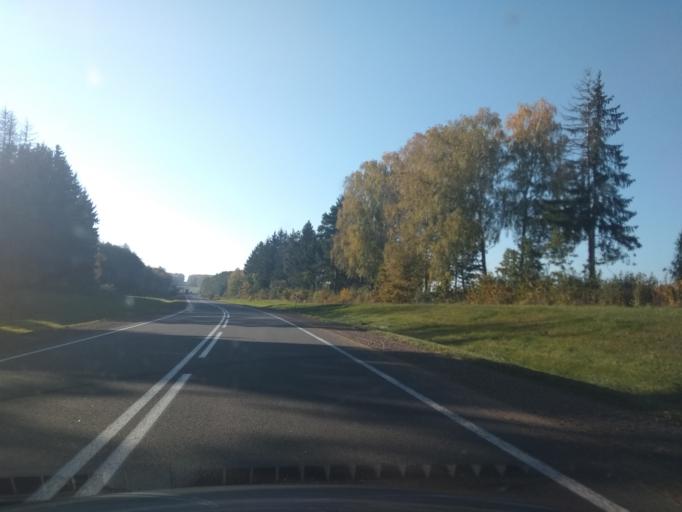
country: BY
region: Grodnenskaya
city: Vyalikaya Byerastavitsa
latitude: 53.1183
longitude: 24.0455
